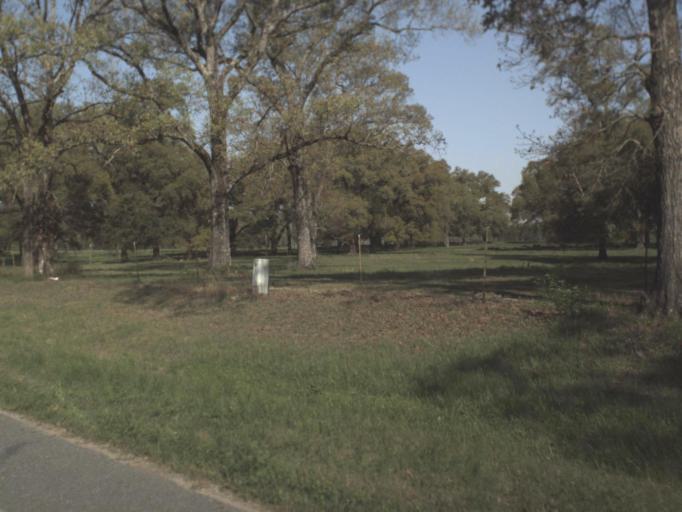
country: US
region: Florida
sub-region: Jackson County
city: Malone
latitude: 30.9570
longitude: -85.1397
